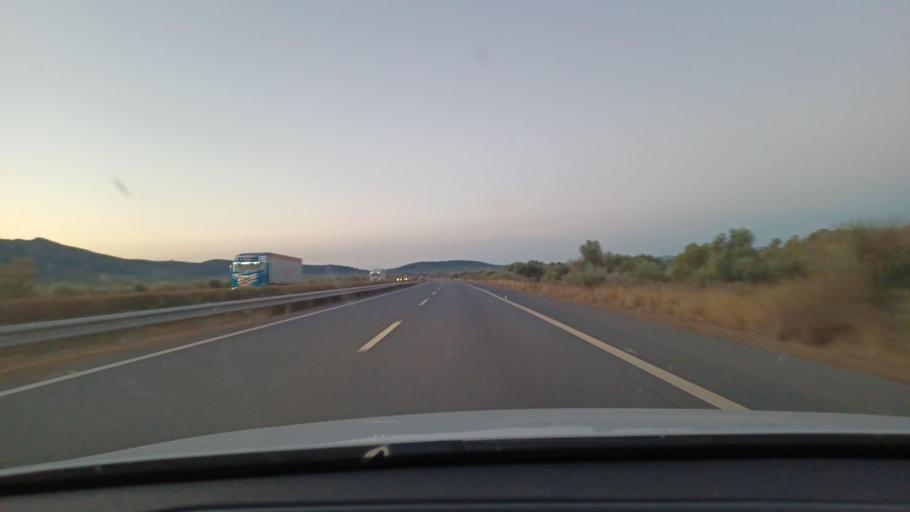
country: ES
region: Catalonia
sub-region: Provincia de Tarragona
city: Ulldecona
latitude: 40.6096
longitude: 0.4746
